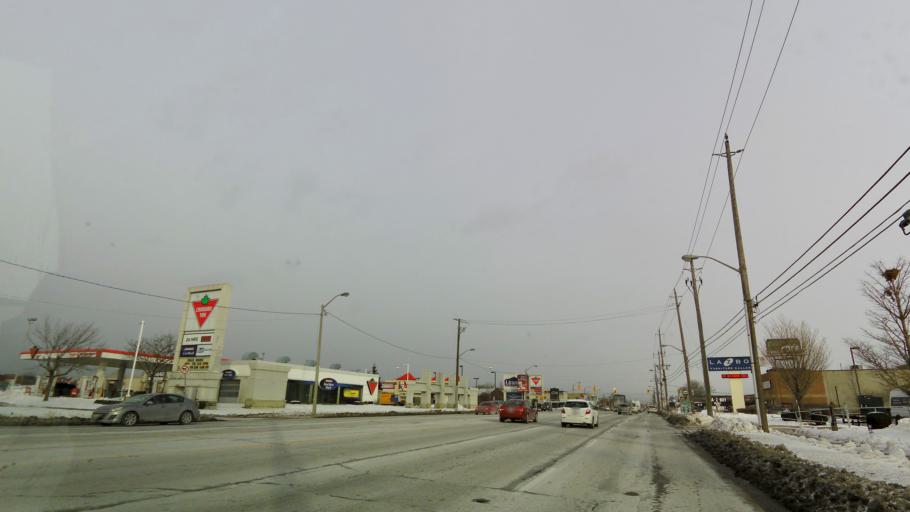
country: CA
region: Ontario
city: Etobicoke
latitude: 43.6166
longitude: -79.5451
